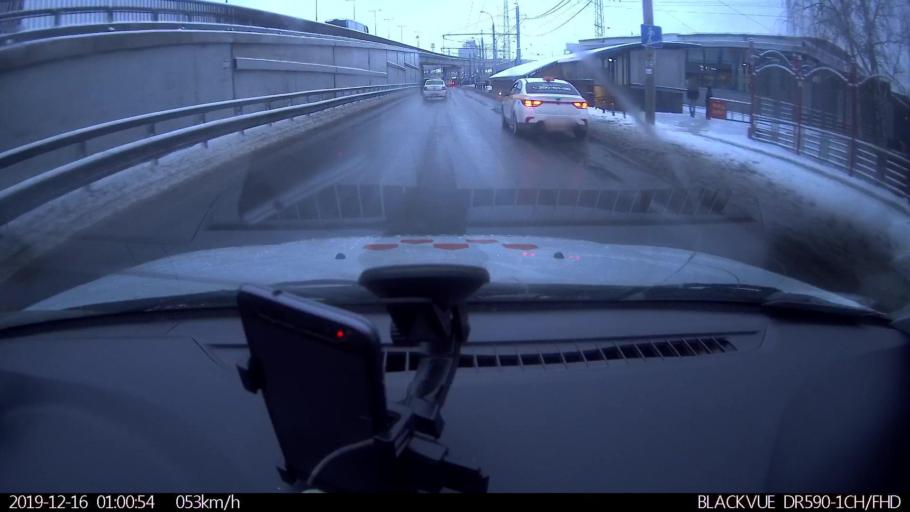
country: RU
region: Nizjnij Novgorod
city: Nizhniy Novgorod
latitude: 56.3223
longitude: 43.9433
